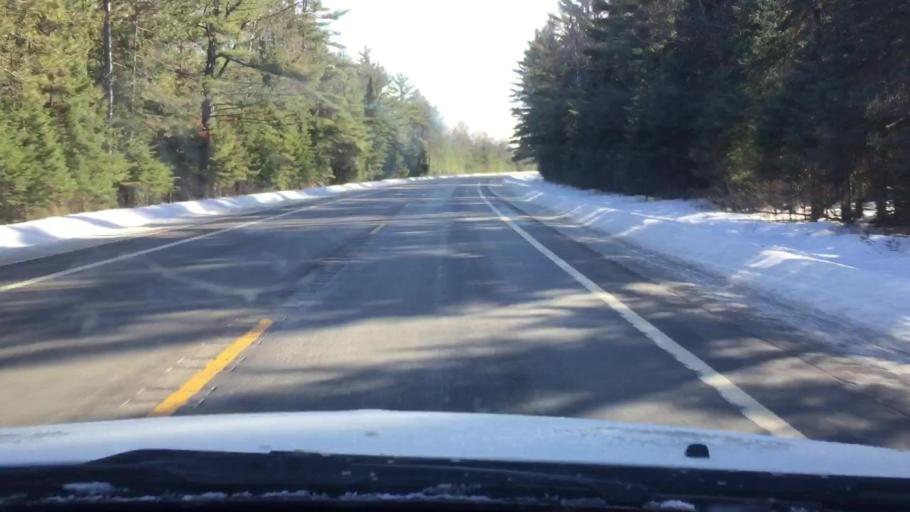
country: US
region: Michigan
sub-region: Charlevoix County
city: East Jordan
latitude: 45.0530
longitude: -85.0715
